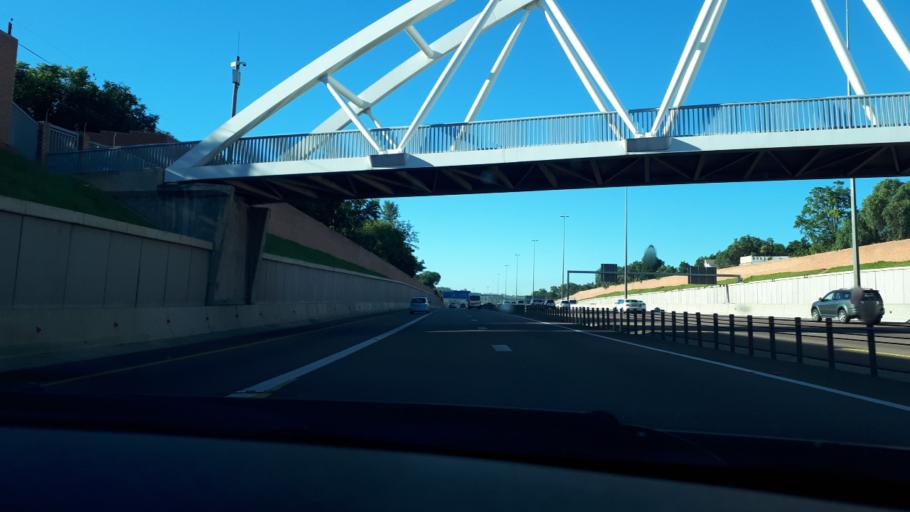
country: ZA
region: Gauteng
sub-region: City of Tshwane Metropolitan Municipality
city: Pretoria
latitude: -25.7689
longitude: 28.2746
